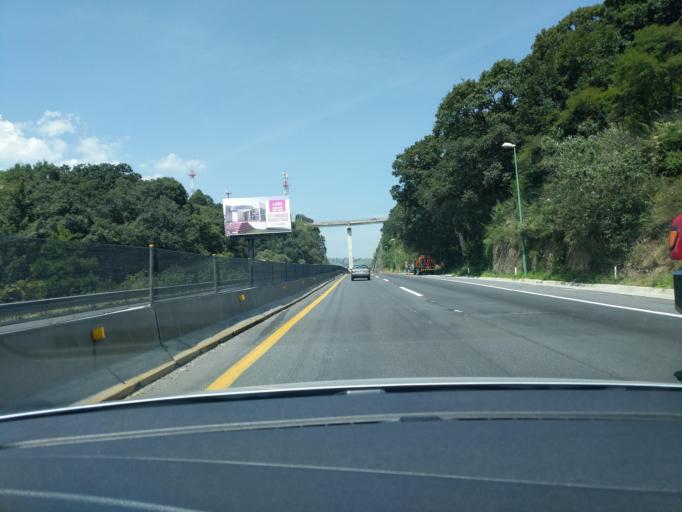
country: MX
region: Mexico
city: San Bartolome Coatepec
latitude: 19.4121
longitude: -99.2974
